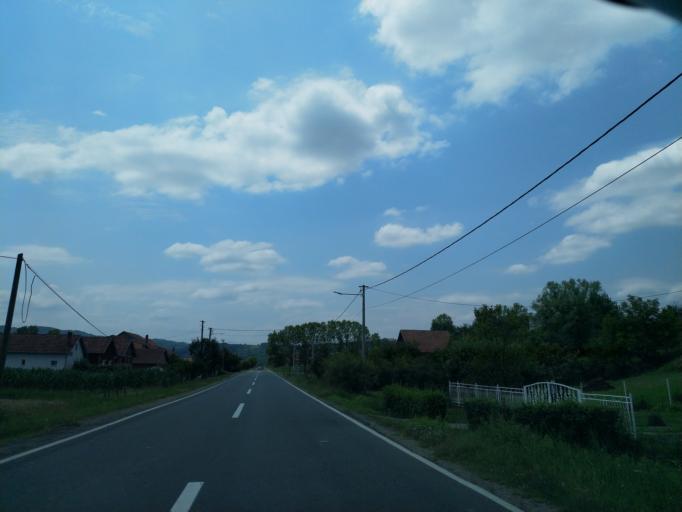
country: RS
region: Central Serbia
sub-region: Toplicki Okrug
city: Blace
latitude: 43.4407
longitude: 21.2235
